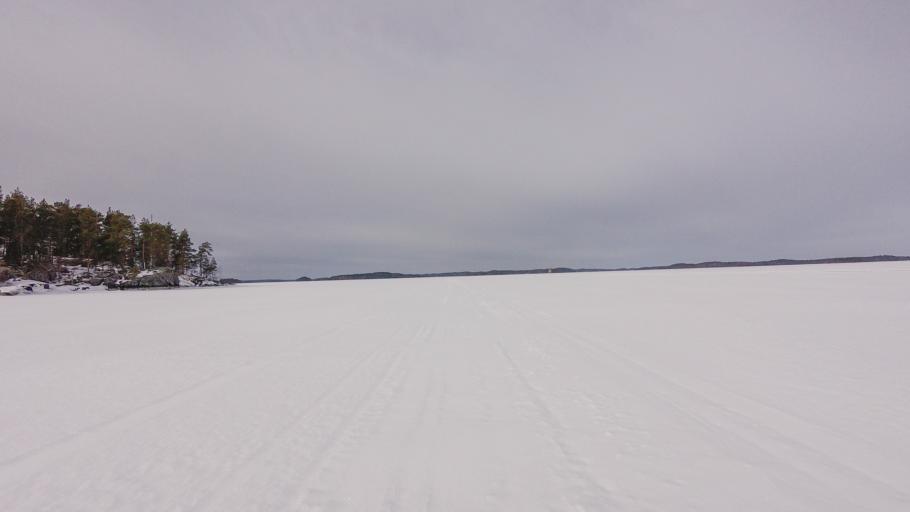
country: FI
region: Southern Savonia
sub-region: Savonlinna
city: Rantasalmi
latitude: 62.1049
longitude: 28.4215
